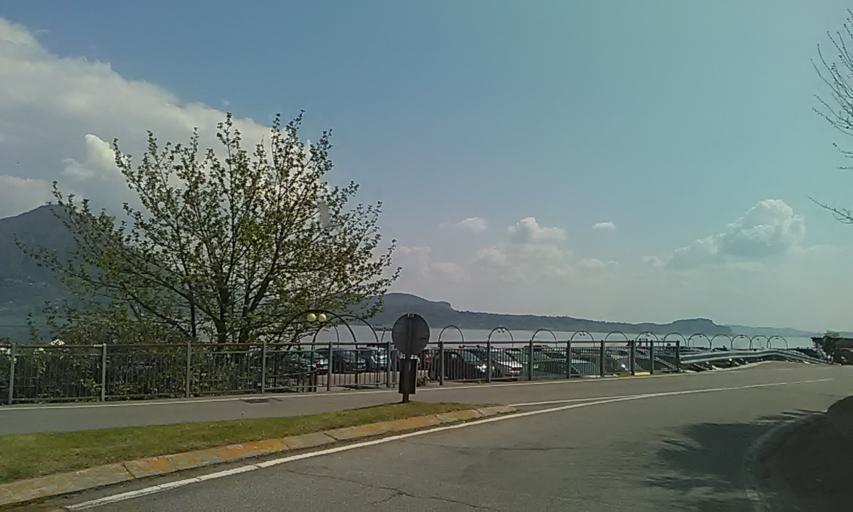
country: IT
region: Piedmont
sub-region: Provincia Verbano-Cusio-Ossola
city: Pallanza-Intra-Suna
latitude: 45.9270
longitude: 8.5657
